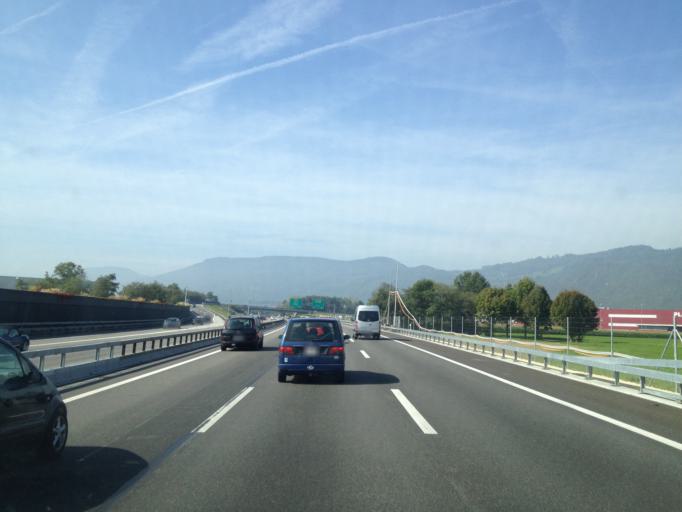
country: CH
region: Solothurn
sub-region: Bezirk Olten
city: Gunzgen
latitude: 47.3120
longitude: 7.8158
